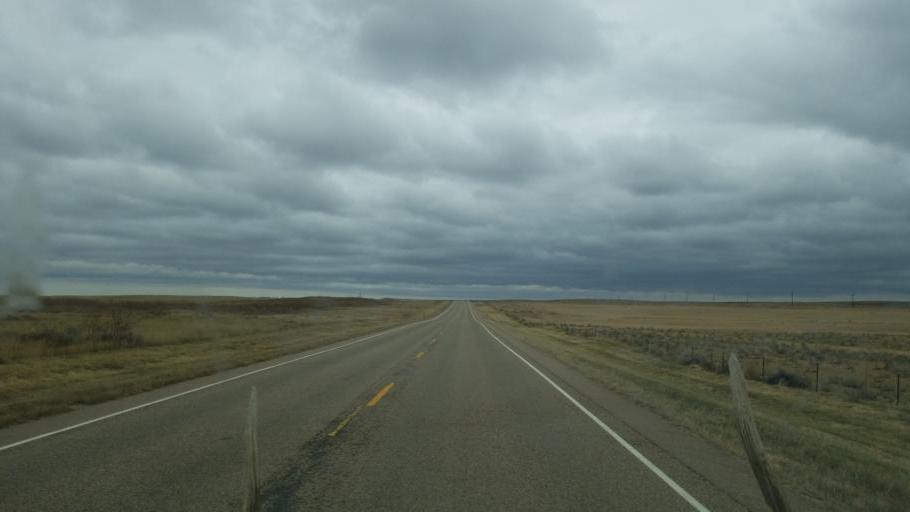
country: US
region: Colorado
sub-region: Kiowa County
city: Eads
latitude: 38.7894
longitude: -102.6785
